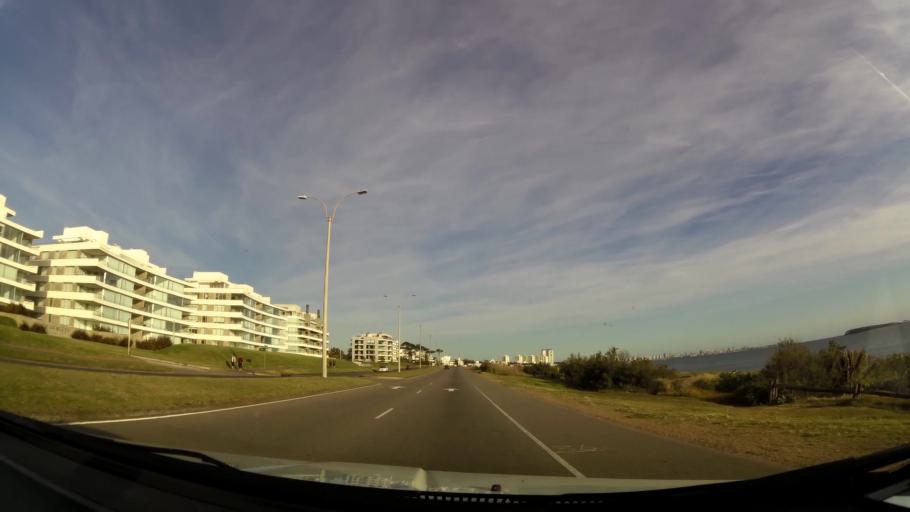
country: UY
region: Maldonado
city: Maldonado
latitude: -34.9156
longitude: -54.9793
